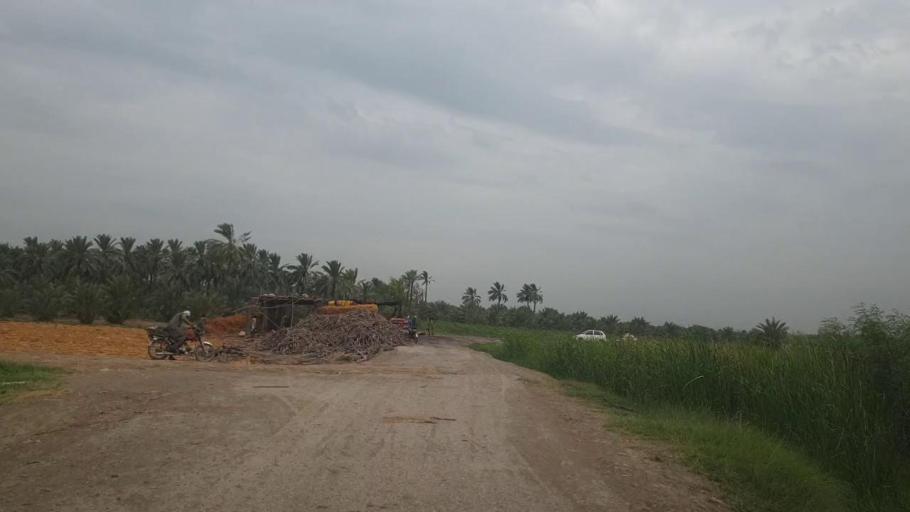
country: PK
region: Sindh
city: Khairpur
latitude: 27.5865
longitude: 68.7392
